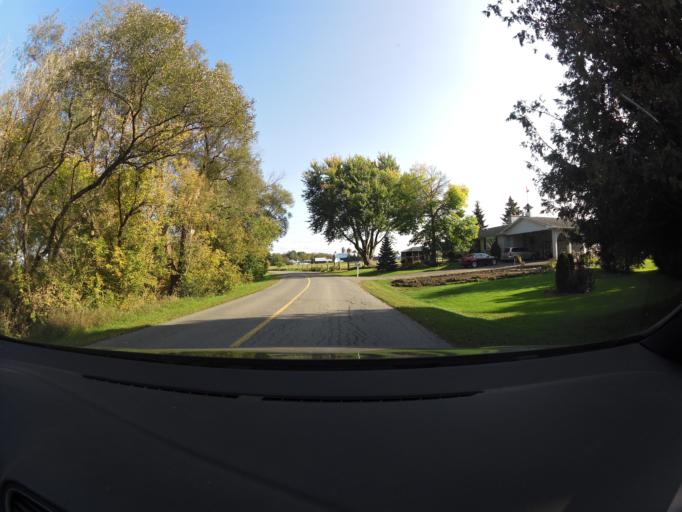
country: CA
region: Ontario
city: Arnprior
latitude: 45.3954
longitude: -76.1950
